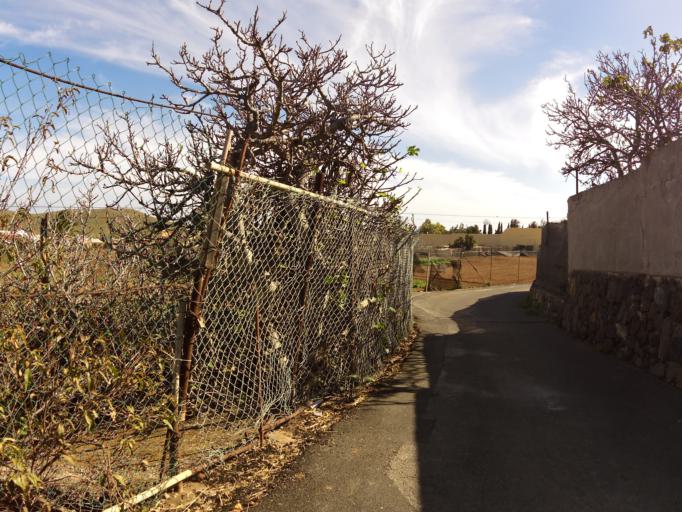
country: ES
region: Canary Islands
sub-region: Provincia de Las Palmas
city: Aguimes
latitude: 27.9062
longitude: -15.4500
